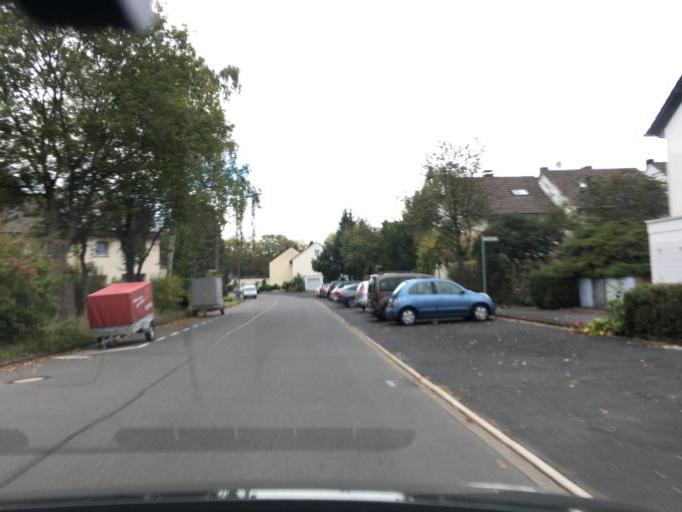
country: DE
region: North Rhine-Westphalia
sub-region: Regierungsbezirk Koln
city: Konigswinter
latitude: 50.6685
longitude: 7.1696
